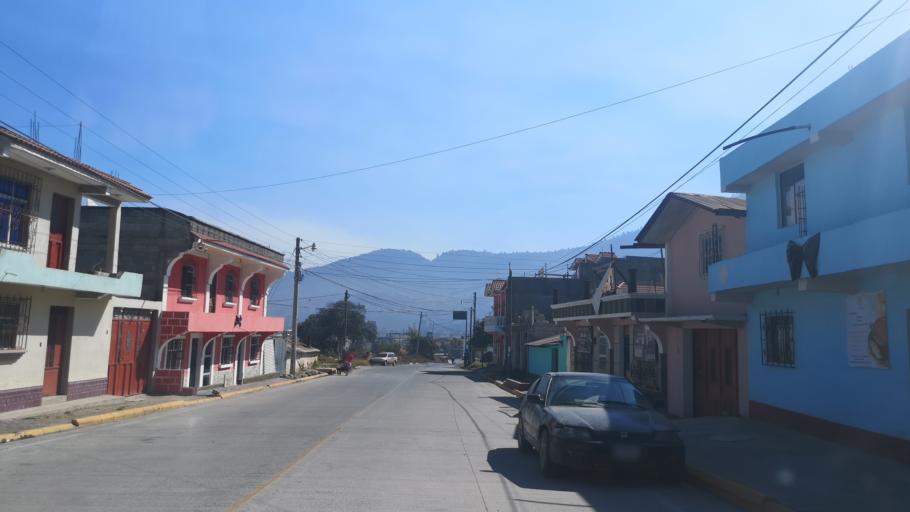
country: GT
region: Quetzaltenango
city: Quetzaltenango
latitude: 14.7993
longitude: -91.5449
